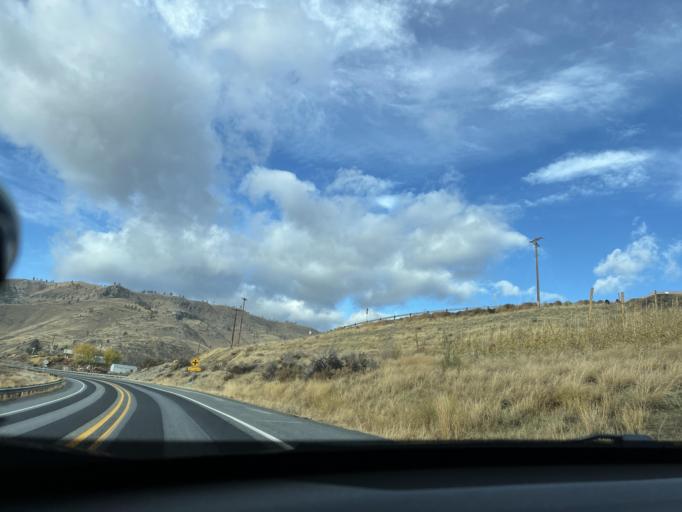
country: US
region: Washington
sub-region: Chelan County
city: Chelan
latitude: 47.8628
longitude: -119.9362
